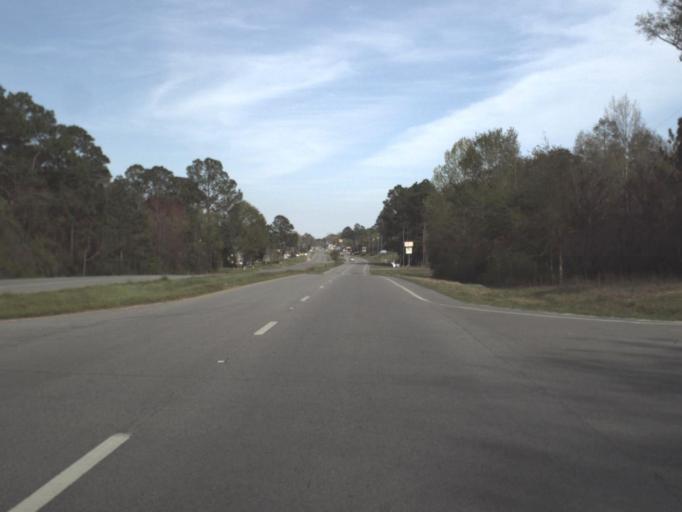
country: US
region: Florida
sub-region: Holmes County
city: Bonifay
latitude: 30.7889
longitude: -85.6952
